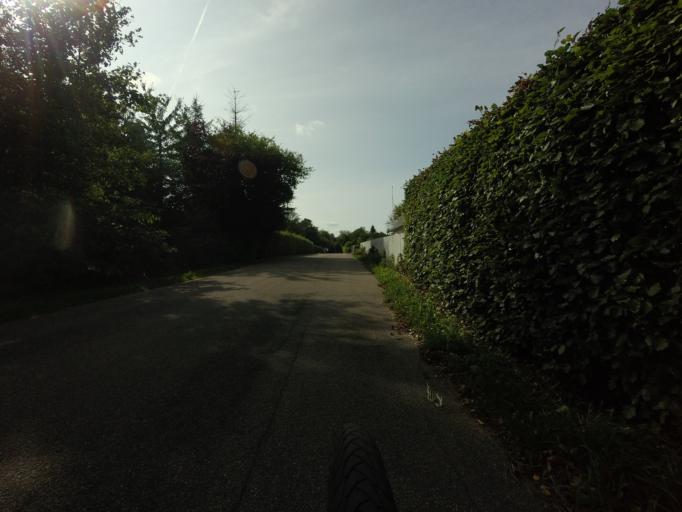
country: DK
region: Zealand
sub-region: Faxe Kommune
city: Fakse Ladeplads
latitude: 55.2087
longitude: 12.1426
